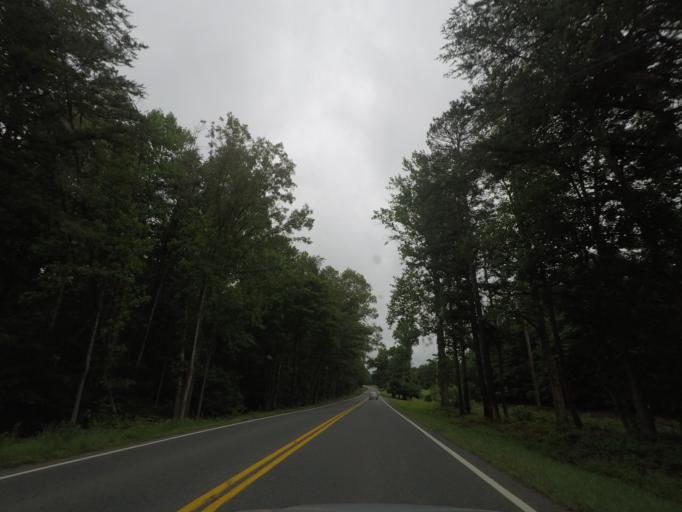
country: US
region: Virginia
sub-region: Fluvanna County
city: Palmyra
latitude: 37.8960
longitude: -78.2596
